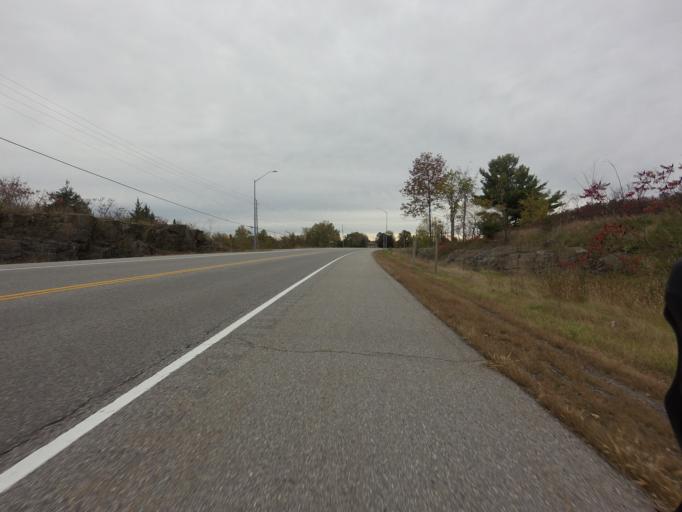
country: CA
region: Ontario
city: Gananoque
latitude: 44.4540
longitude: -76.2674
